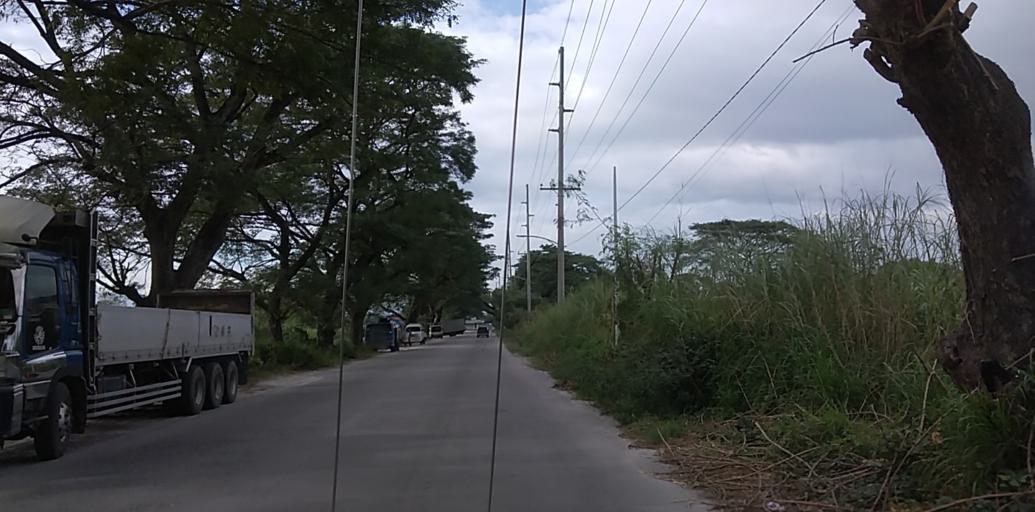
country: PH
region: Central Luzon
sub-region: Province of Pampanga
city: Porac
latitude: 15.0780
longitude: 120.5491
